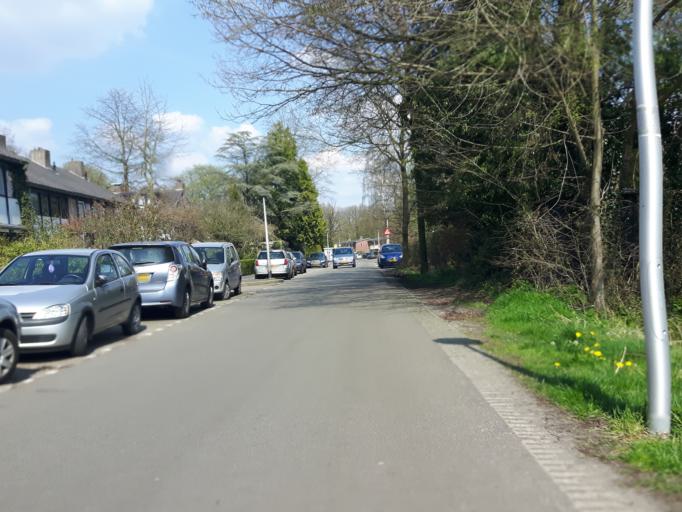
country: NL
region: Overijssel
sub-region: Gemeente Hengelo
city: Hengelo
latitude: 52.2012
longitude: 6.8002
